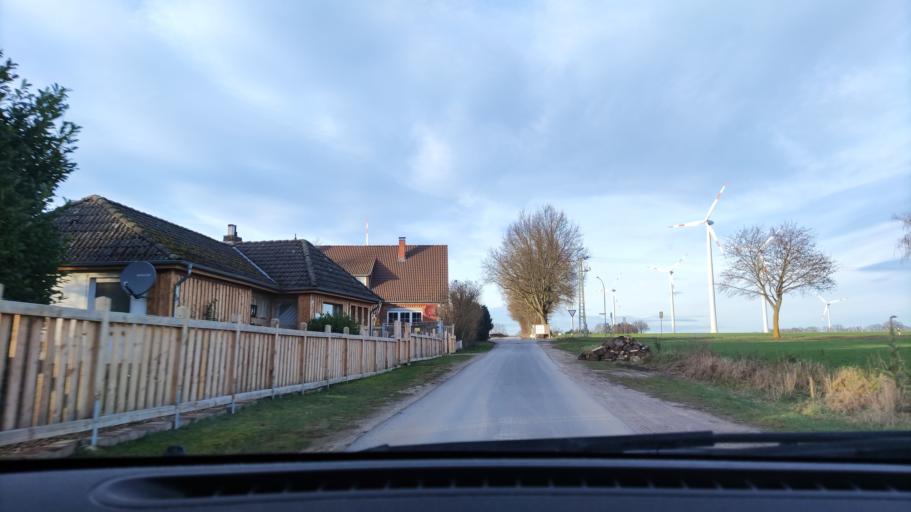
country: DE
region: Lower Saxony
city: Wriedel
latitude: 53.0383
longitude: 10.3305
